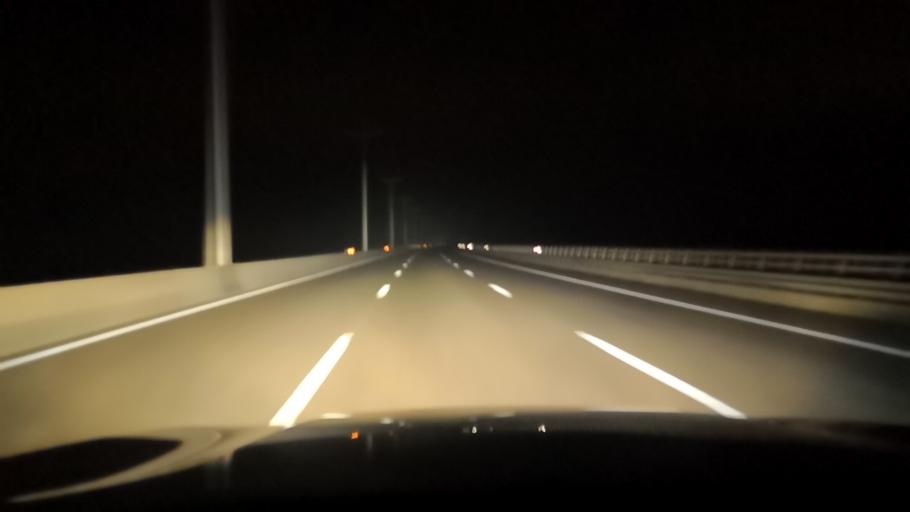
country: PT
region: Lisbon
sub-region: Vila Franca de Xira
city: Castanheira do Ribatejo
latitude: 39.0069
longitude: -8.9159
